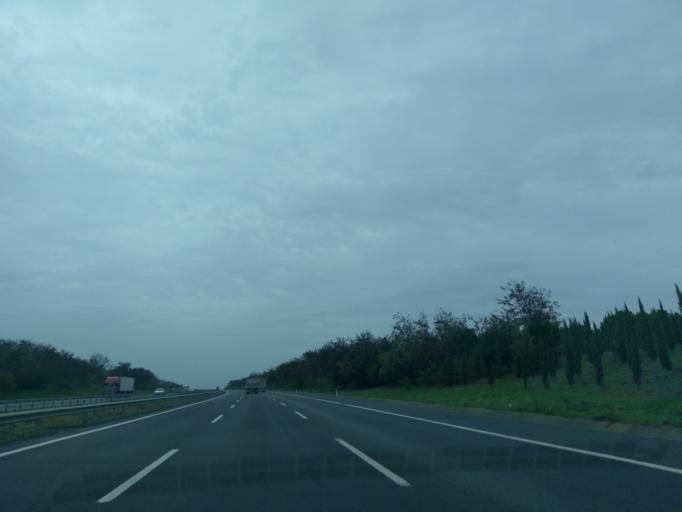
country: TR
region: Istanbul
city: Canta
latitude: 41.1613
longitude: 28.1356
